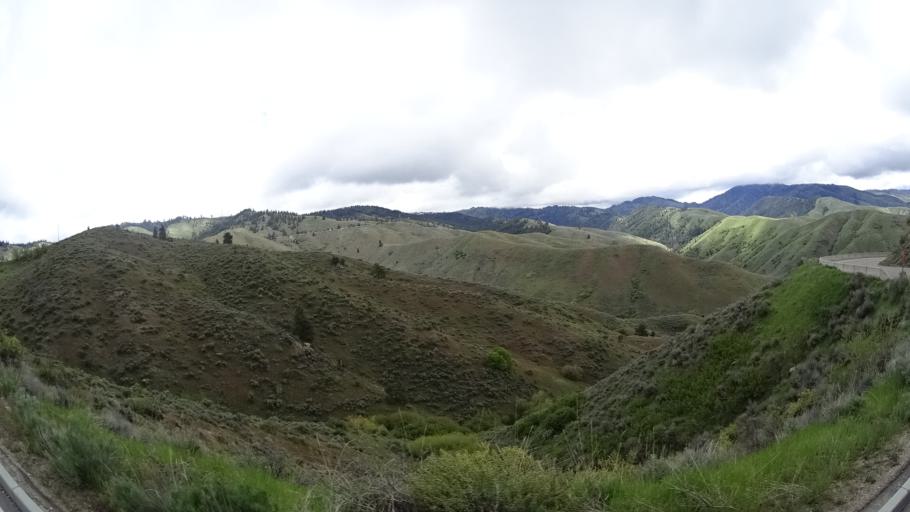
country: US
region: Idaho
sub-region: Ada County
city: Boise
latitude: 43.7202
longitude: -116.1605
